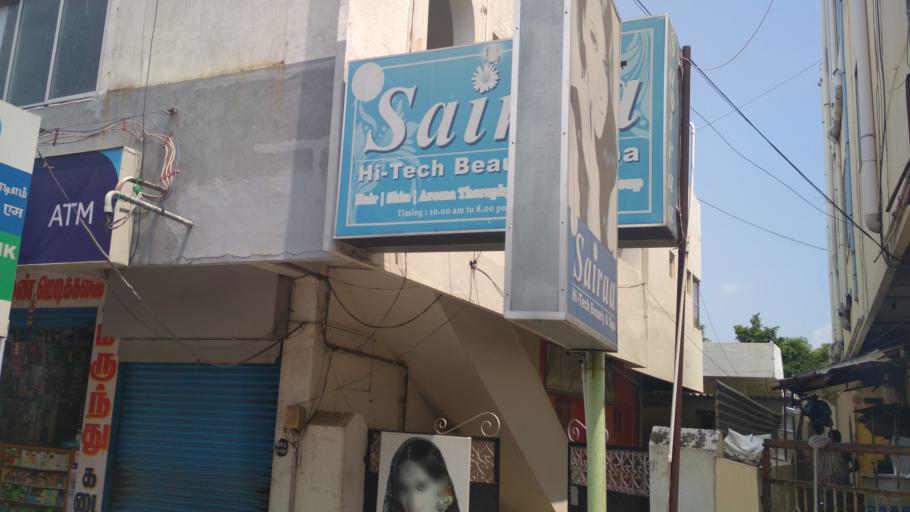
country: IN
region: Tamil Nadu
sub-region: Coimbatore
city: Coimbatore
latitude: 11.0257
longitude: 76.9395
